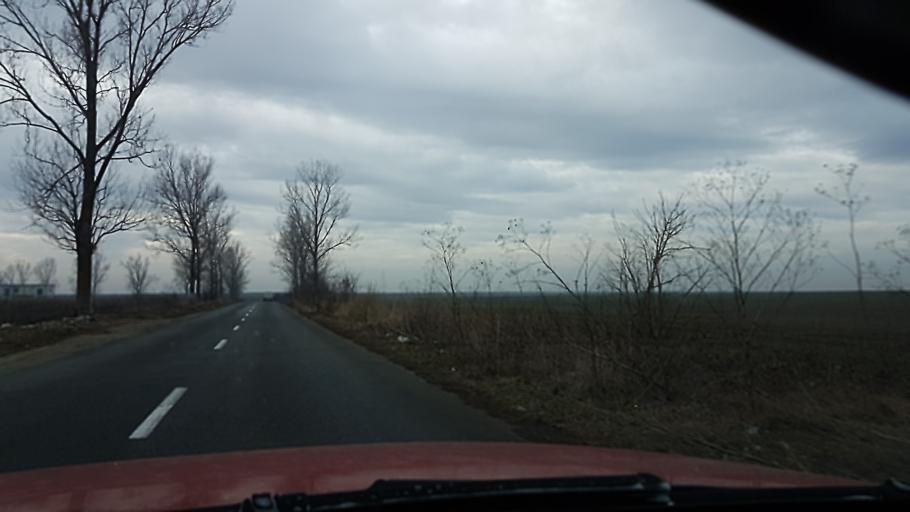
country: RO
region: Giurgiu
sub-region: Comuna Herasti
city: Herasti
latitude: 44.2465
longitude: 26.3629
